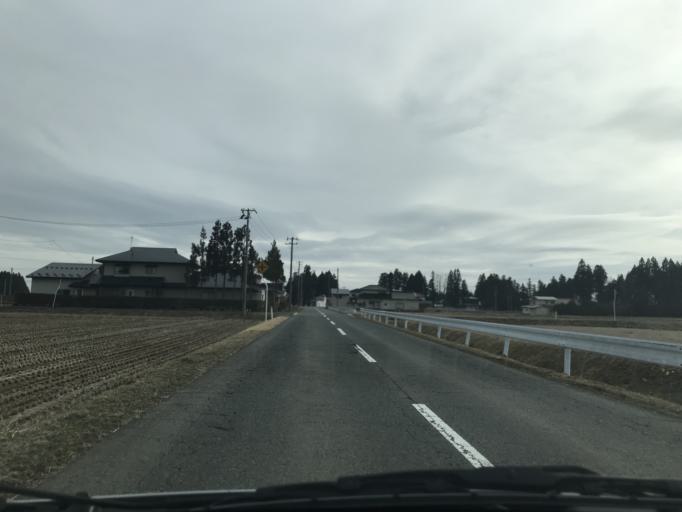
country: JP
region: Iwate
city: Hanamaki
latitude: 39.3680
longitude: 141.0687
